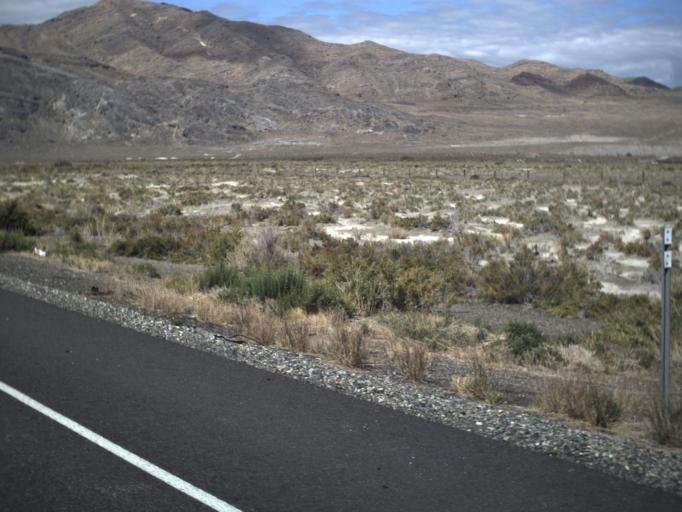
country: US
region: Utah
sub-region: Tooele County
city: Wendover
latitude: 40.7459
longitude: -113.9934
